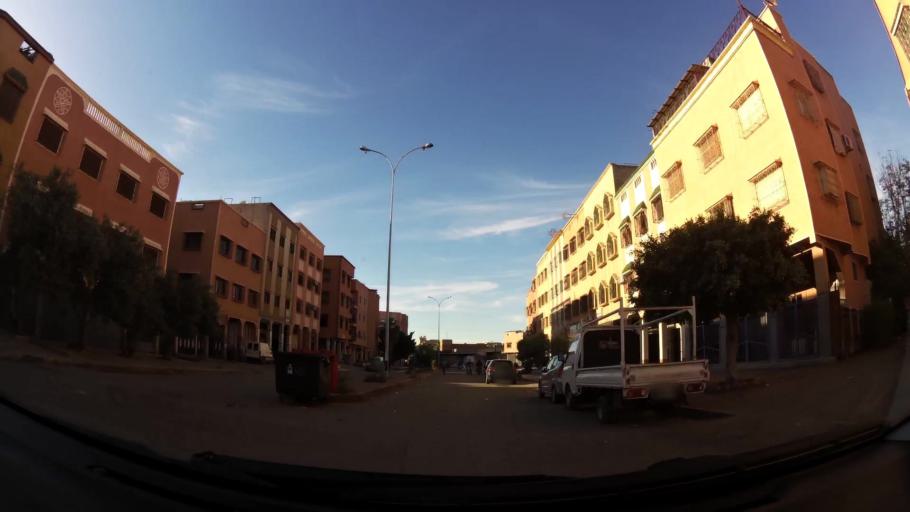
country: MA
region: Marrakech-Tensift-Al Haouz
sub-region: Marrakech
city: Marrakesh
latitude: 31.6155
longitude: -8.0586
